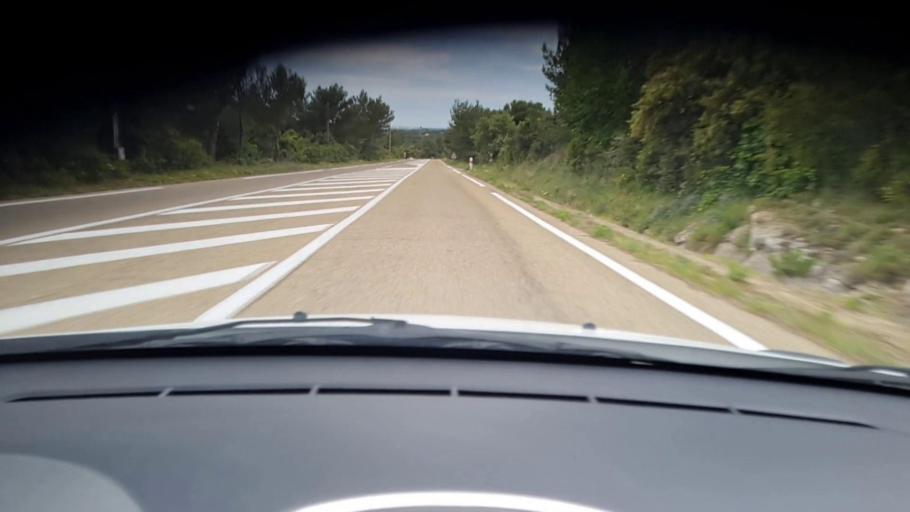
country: FR
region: Languedoc-Roussillon
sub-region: Departement du Gard
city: Nimes
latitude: 43.8738
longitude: 4.3790
